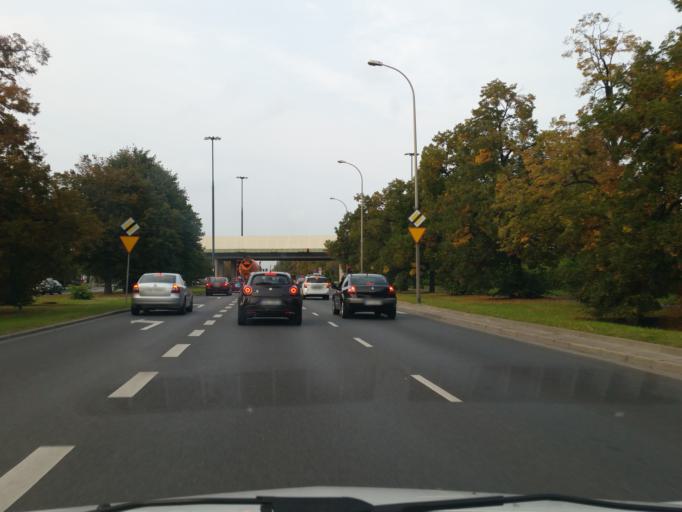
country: PL
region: Masovian Voivodeship
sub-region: Warszawa
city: Wlochy
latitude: 52.1822
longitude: 20.9785
